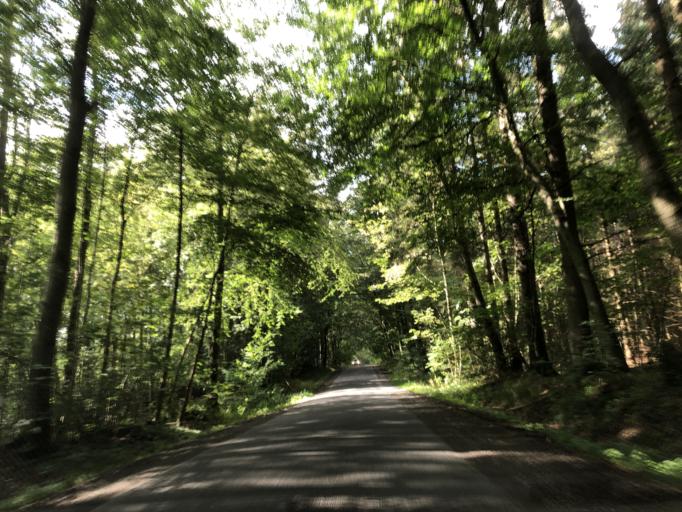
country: DK
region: Central Jutland
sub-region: Skanderborg Kommune
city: Galten
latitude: 56.1742
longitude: 9.9244
